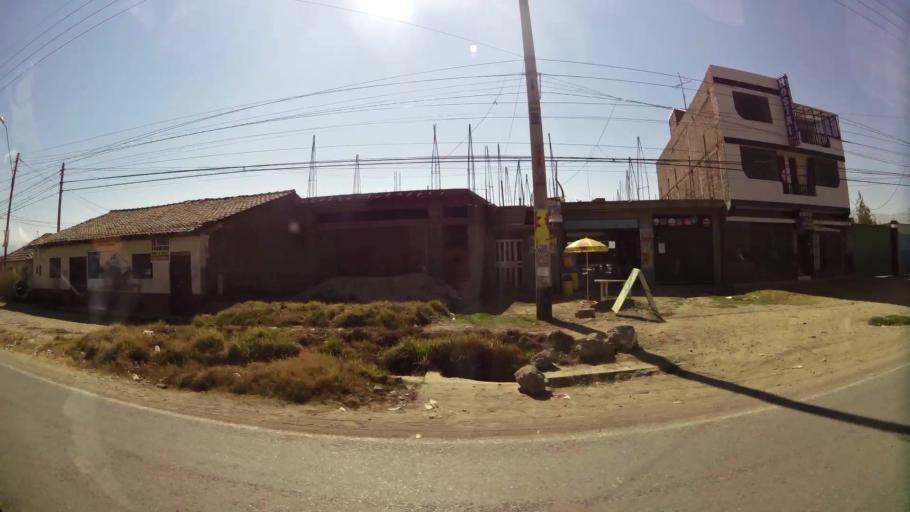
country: PE
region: Junin
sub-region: Provincia de Huancayo
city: San Agustin
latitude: -12.0032
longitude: -75.2507
